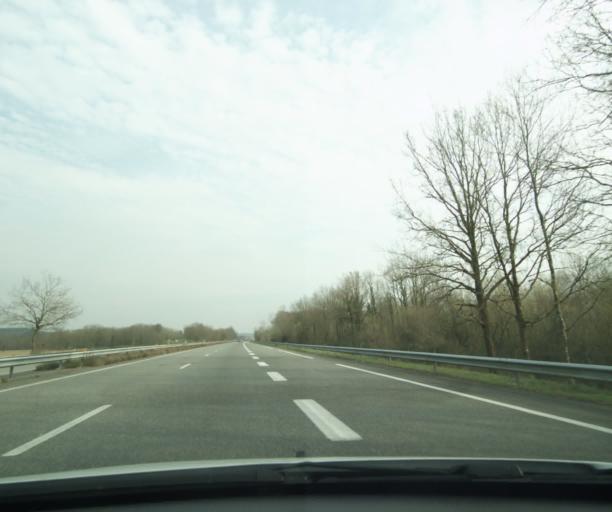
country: FR
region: Aquitaine
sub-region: Departement des Pyrenees-Atlantiques
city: Mourenx
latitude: 43.4203
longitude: -0.5912
